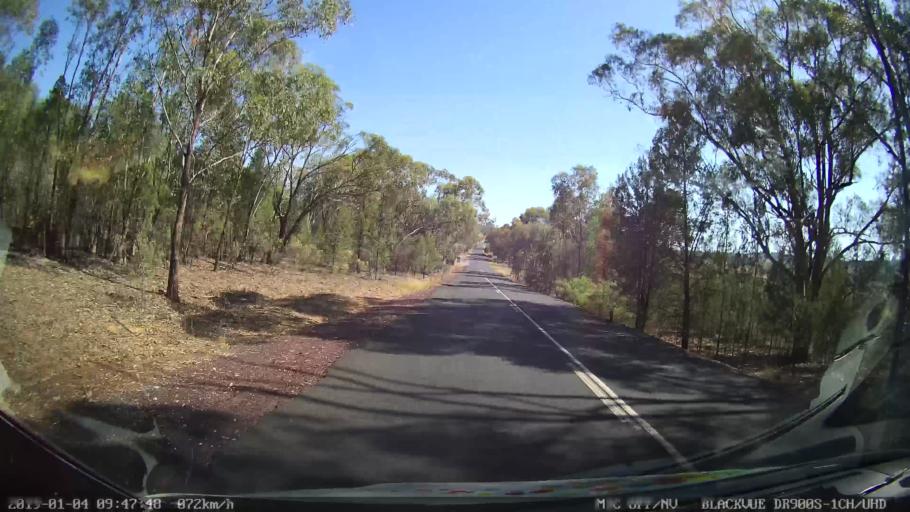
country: AU
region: New South Wales
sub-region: Cabonne
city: Canowindra
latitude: -33.6028
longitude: 148.4317
